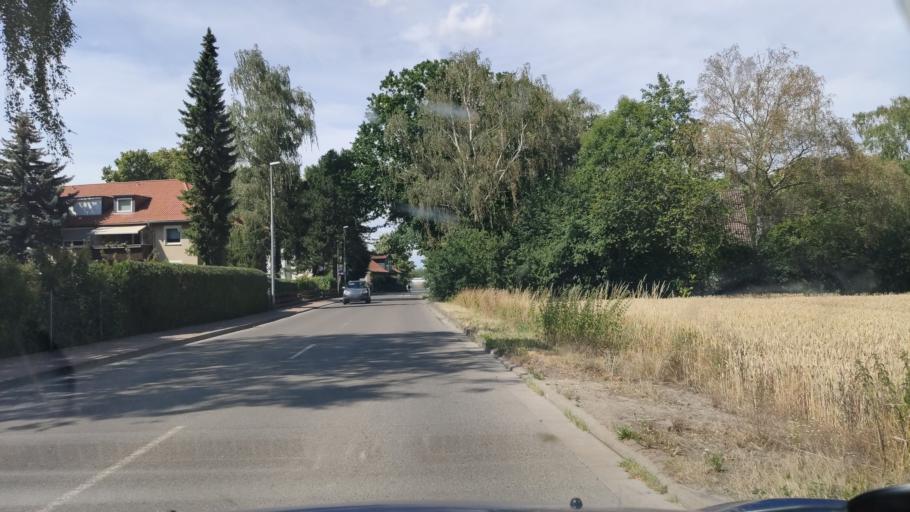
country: DE
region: Lower Saxony
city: Ronnenberg
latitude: 52.3418
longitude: 9.6543
